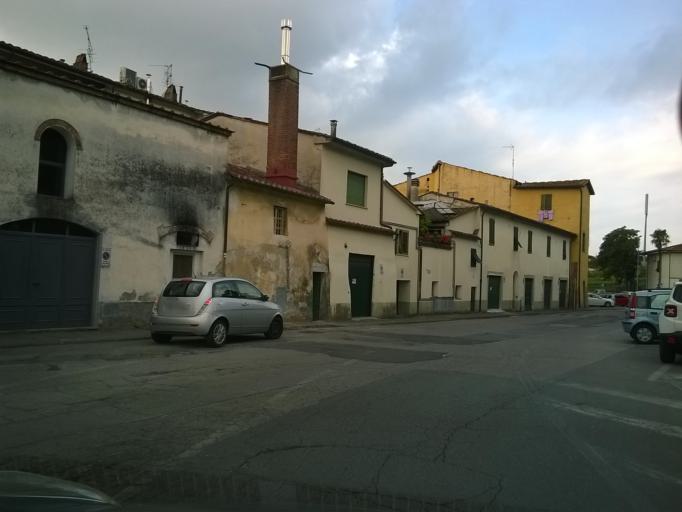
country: IT
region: Tuscany
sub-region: Provincia di Pistoia
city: Borgo a Buggiano
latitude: 43.8805
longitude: 10.7284
